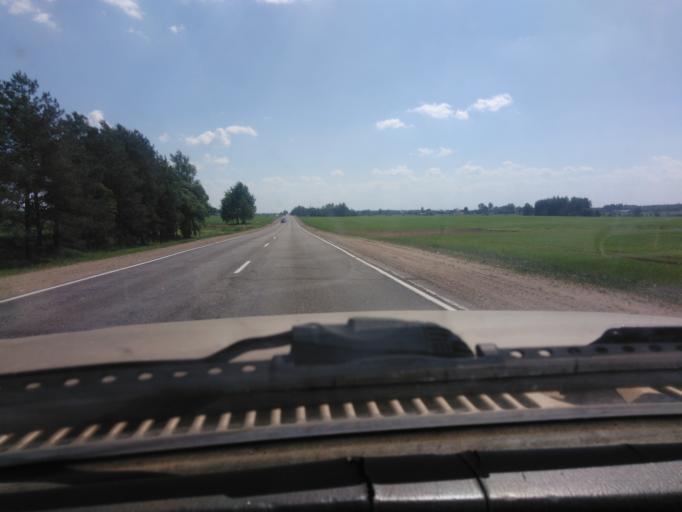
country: BY
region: Mogilev
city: Kamyennyya Lavy
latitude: 54.0438
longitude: 30.3250
